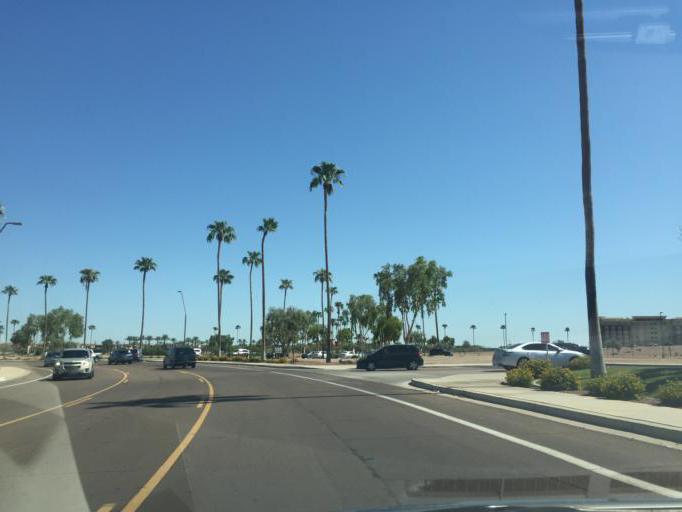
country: US
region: Arizona
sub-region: Maricopa County
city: Guadalupe
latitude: 33.3377
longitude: -111.9693
